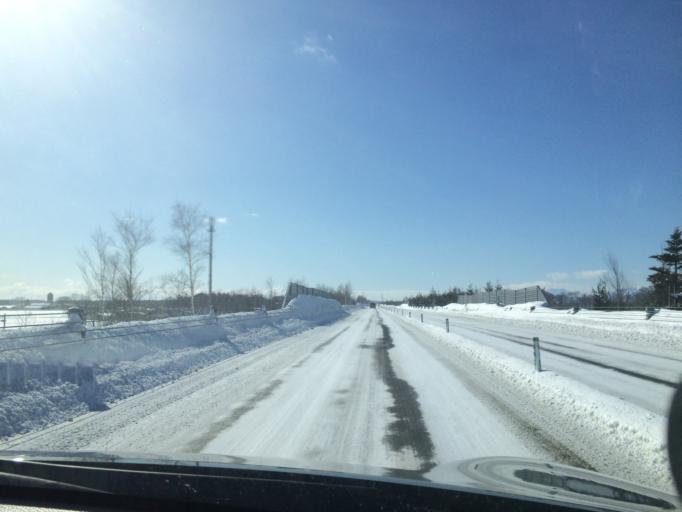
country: JP
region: Hokkaido
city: Chitose
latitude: 42.8794
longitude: 141.6189
